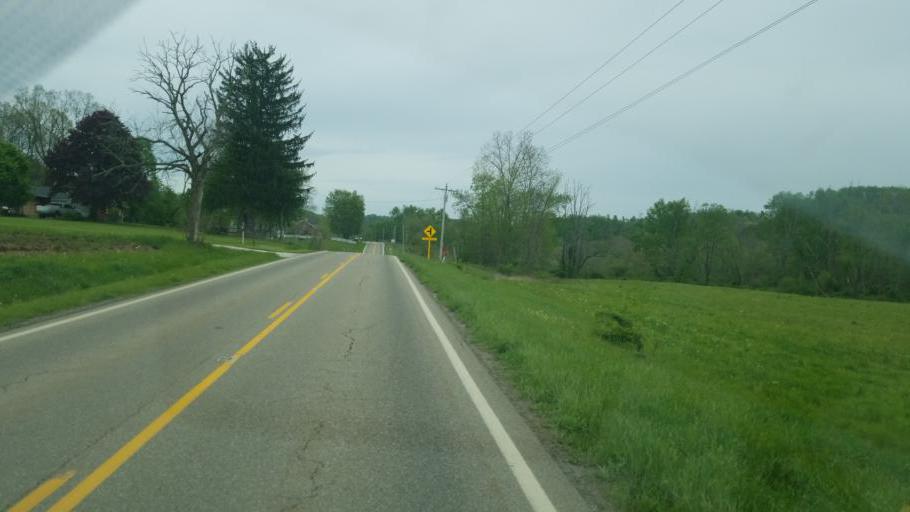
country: US
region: Ohio
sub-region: Tuscarawas County
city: Newcomerstown
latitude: 40.2578
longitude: -81.5126
